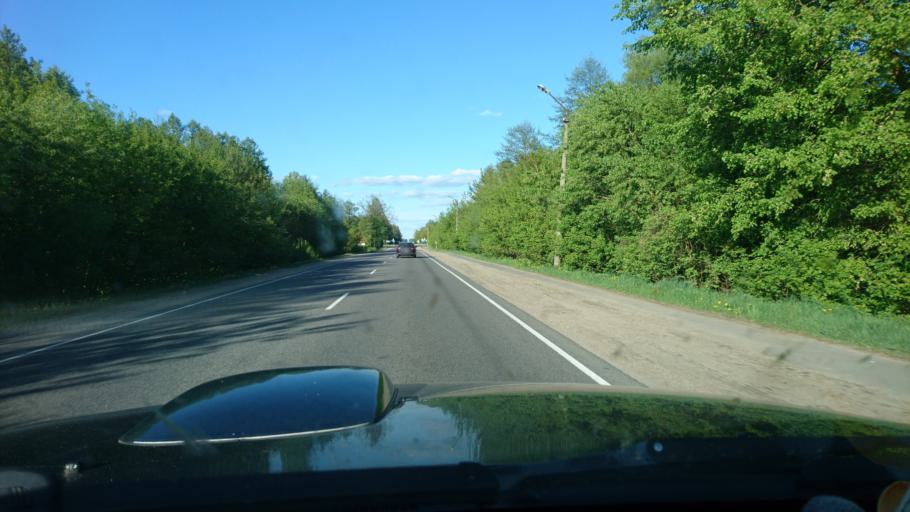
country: BY
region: Brest
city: Byaroza
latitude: 52.5441
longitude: 25.0045
